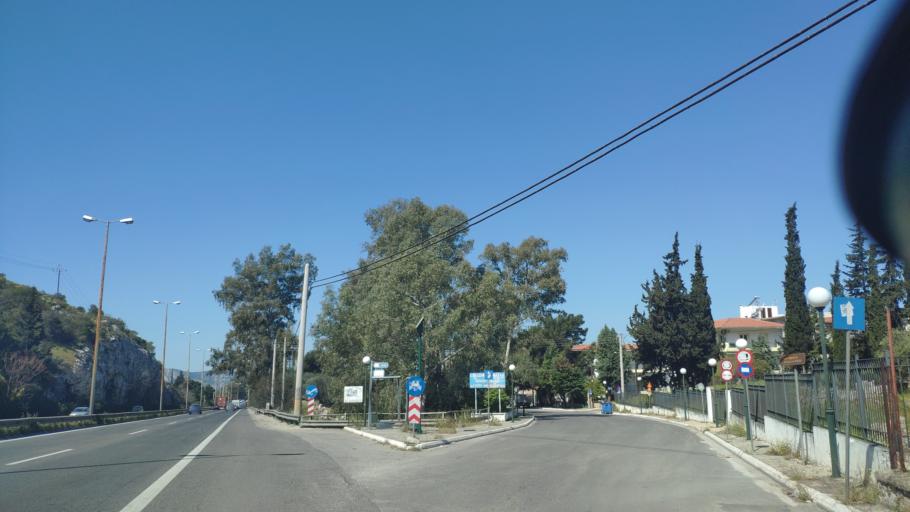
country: GR
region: Attica
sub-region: Nomarchia Athinas
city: Skaramangas
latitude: 38.0123
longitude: 23.6163
